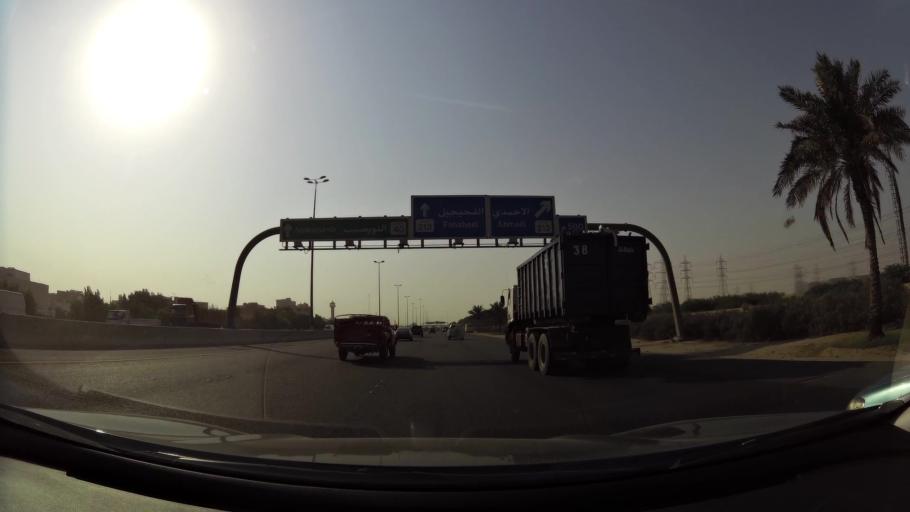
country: KW
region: Al Ahmadi
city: Al Ahmadi
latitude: 29.1017
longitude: 48.0965
